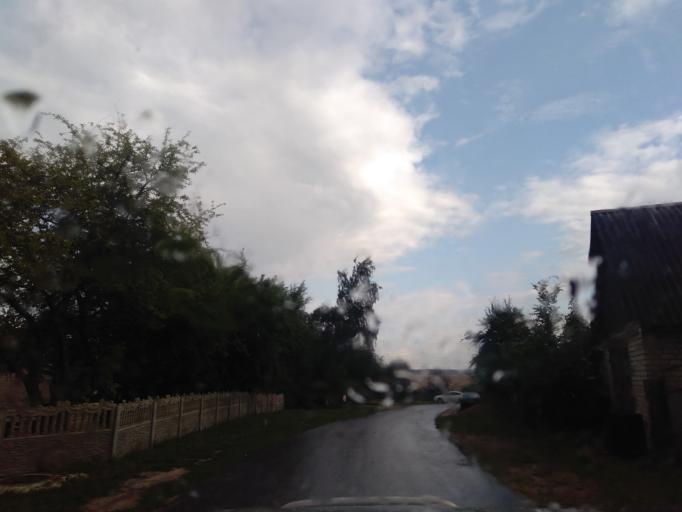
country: BY
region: Minsk
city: Kapyl'
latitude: 53.1458
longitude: 27.1153
